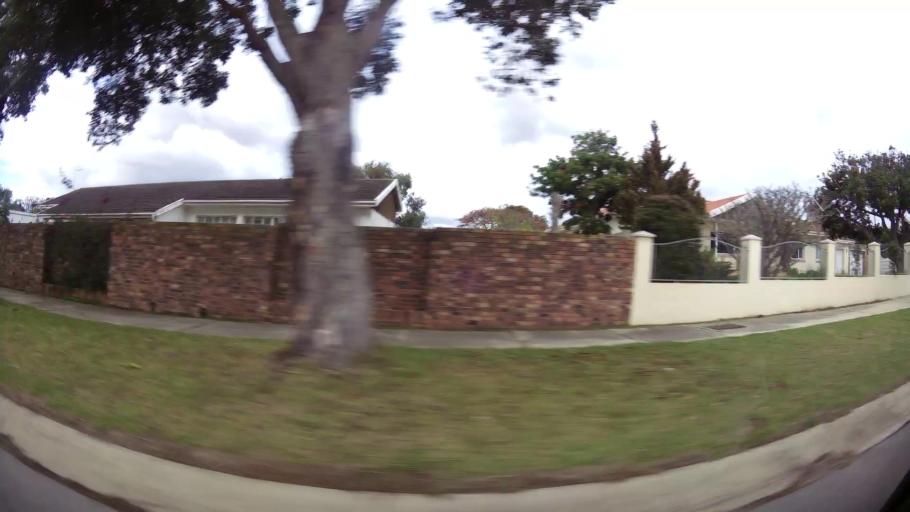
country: ZA
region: Eastern Cape
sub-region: Nelson Mandela Bay Metropolitan Municipality
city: Port Elizabeth
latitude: -33.9371
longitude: 25.5217
